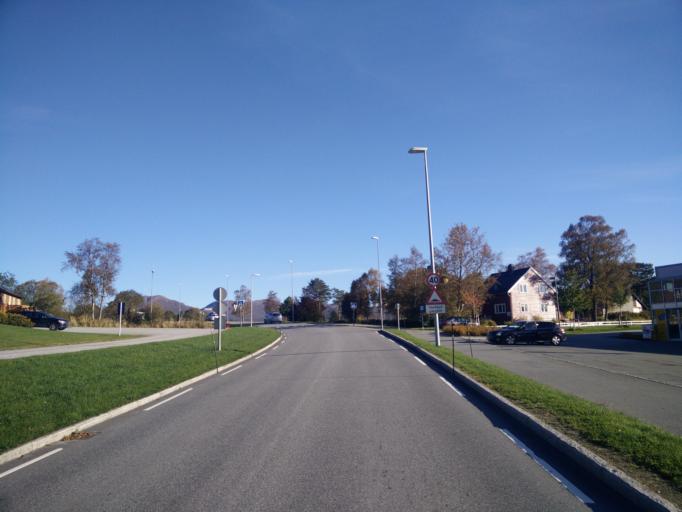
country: NO
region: More og Romsdal
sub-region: Halsa
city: Liaboen
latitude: 63.1194
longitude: 8.3094
